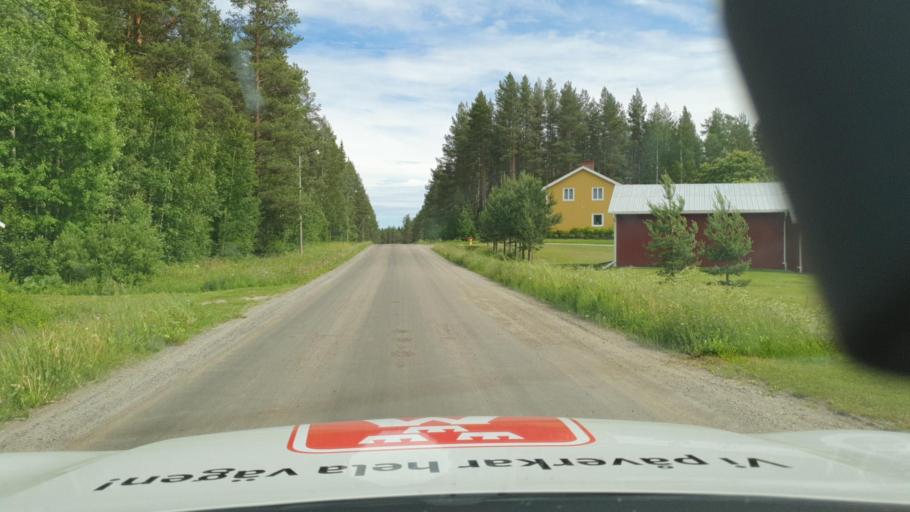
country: SE
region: Vaesterbotten
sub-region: Skelleftea Kommun
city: Burtraesk
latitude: 64.4886
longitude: 20.6123
